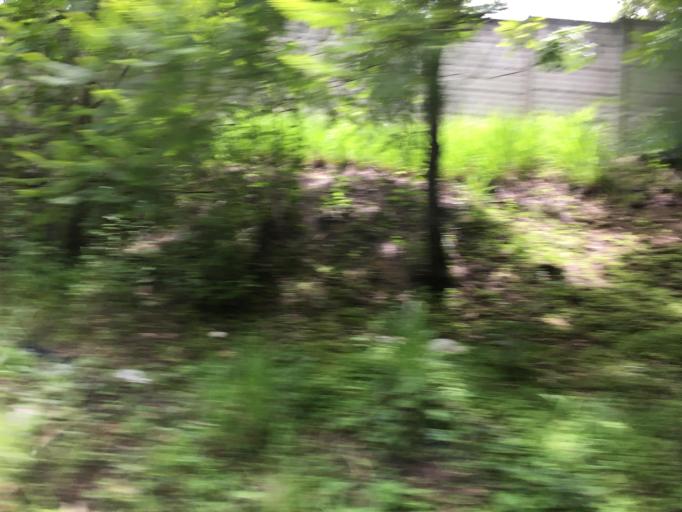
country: GT
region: Guatemala
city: Amatitlan
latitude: 14.4997
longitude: -90.6185
